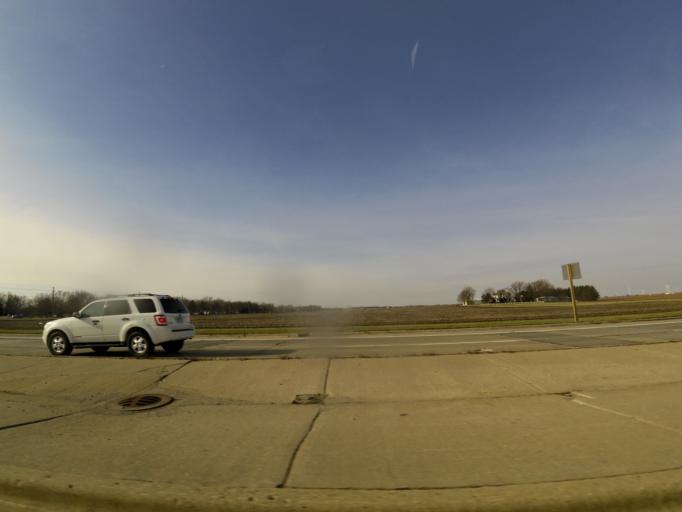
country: US
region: Illinois
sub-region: Macon County
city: Forsyth
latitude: 39.9363
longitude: -88.9557
